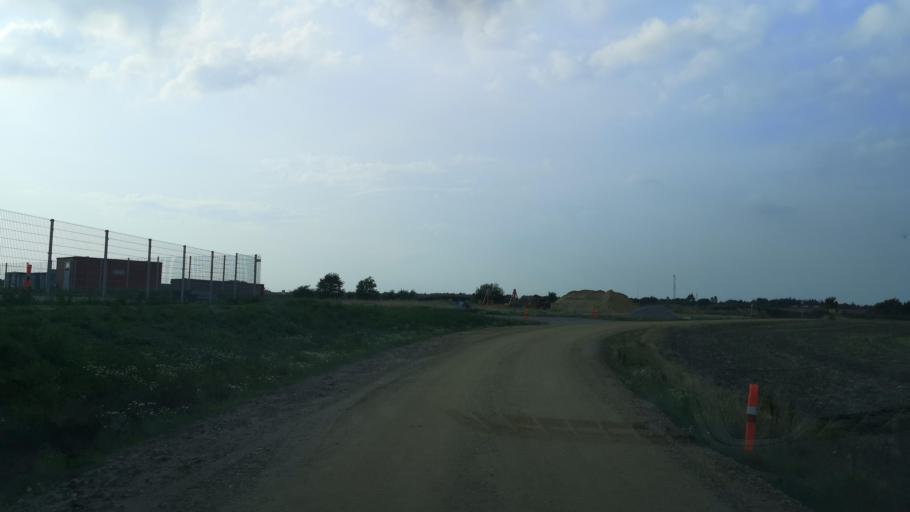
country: DK
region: Central Jutland
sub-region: Herning Kommune
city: Snejbjerg
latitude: 56.1270
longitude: 8.9234
